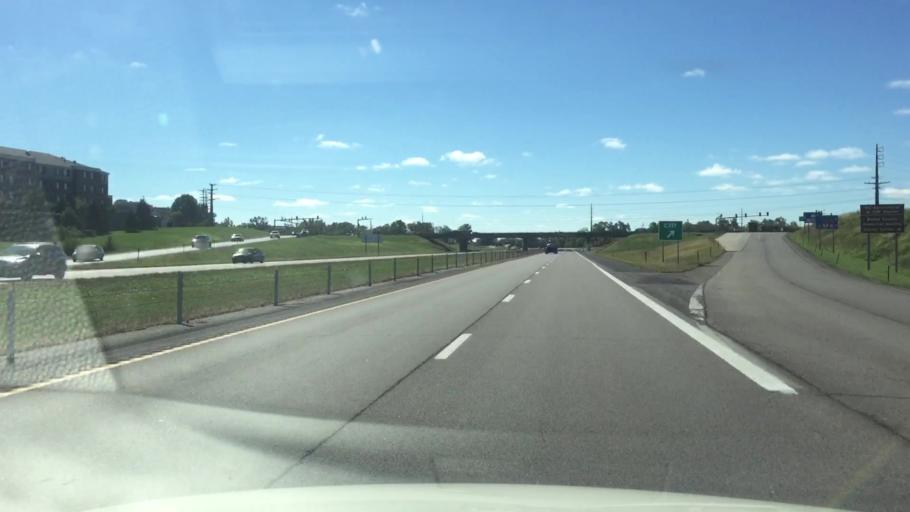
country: US
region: Missouri
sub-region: Boone County
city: Columbia
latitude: 38.9157
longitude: -92.2939
